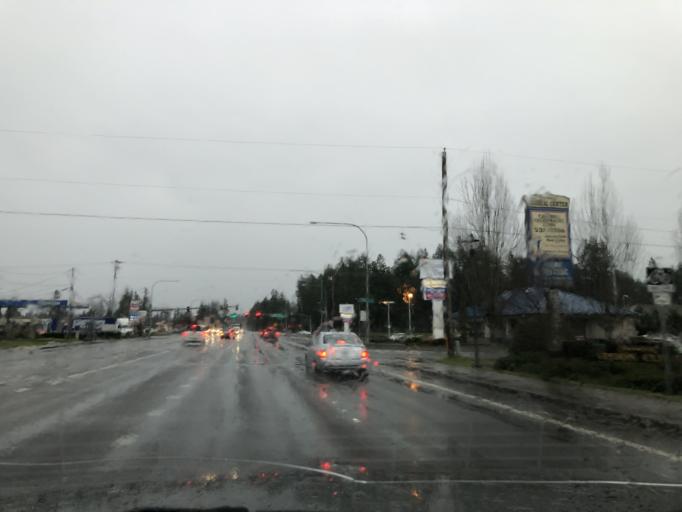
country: US
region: Washington
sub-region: Pierce County
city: Spanaway
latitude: 47.0987
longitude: -122.4349
